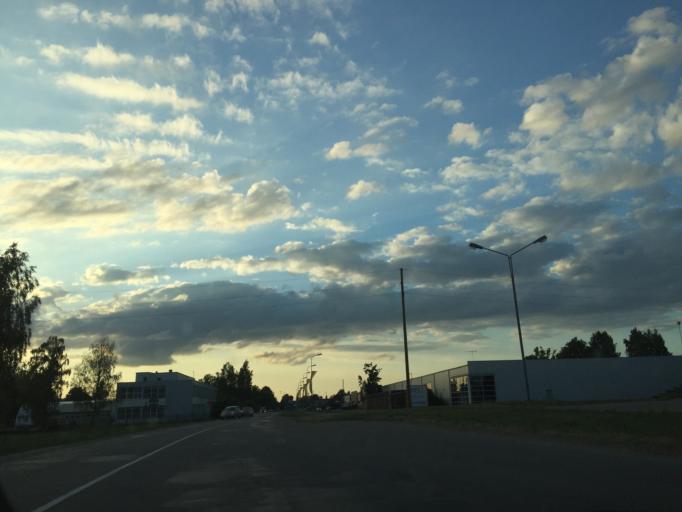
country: LV
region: Sigulda
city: Sigulda
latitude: 57.1419
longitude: 24.8608
